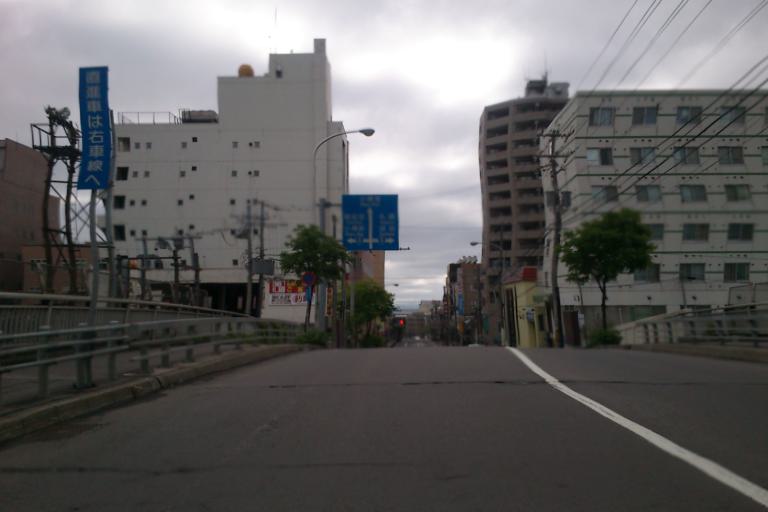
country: JP
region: Hokkaido
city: Otaru
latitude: 43.1946
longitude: 140.9944
